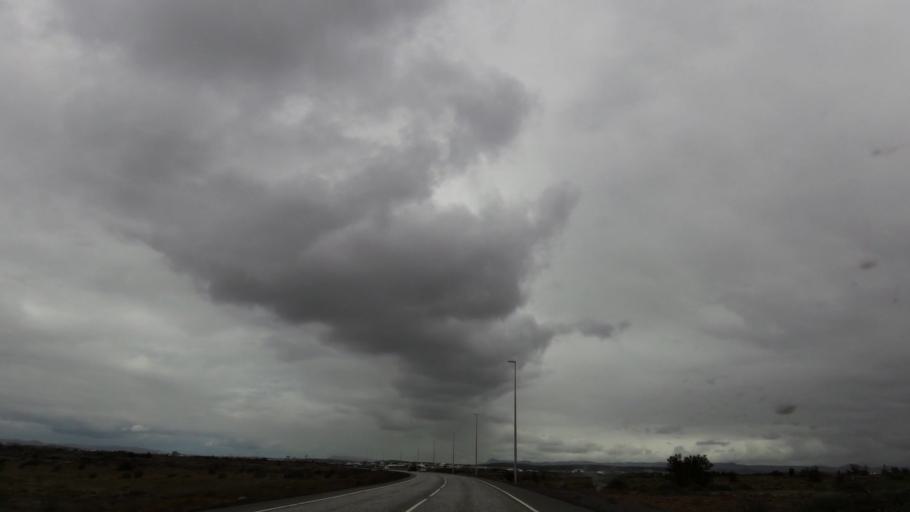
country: IS
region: Capital Region
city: Alftanes
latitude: 64.0909
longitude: -21.9837
